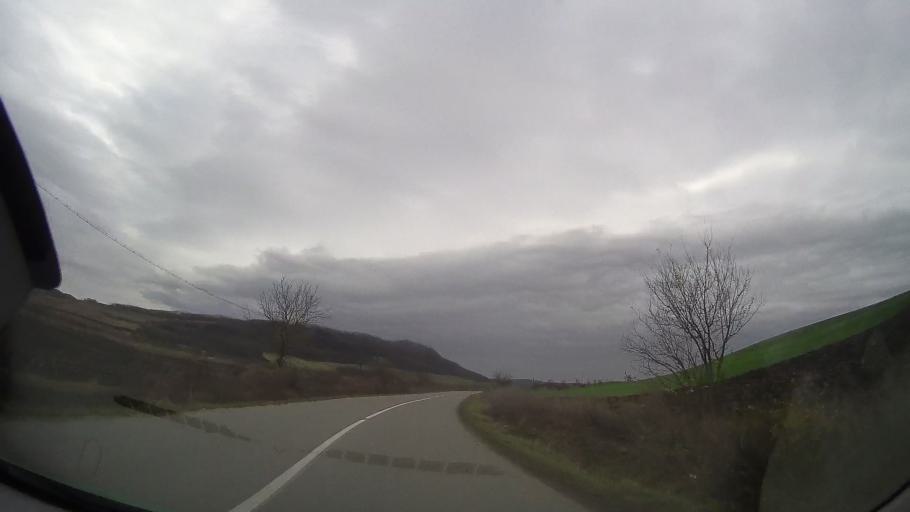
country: RO
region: Bistrita-Nasaud
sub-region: Comuna Milas
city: Milas
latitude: 46.8019
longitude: 24.4278
